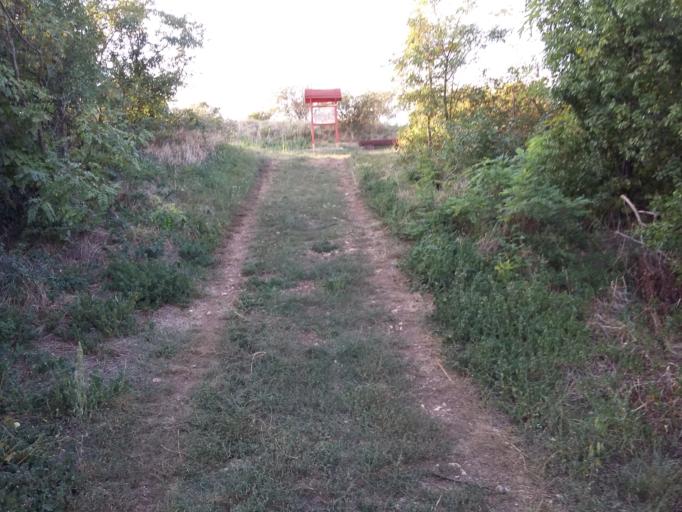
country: HU
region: Borsod-Abauj-Zemplen
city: Bekecs
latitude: 48.1559
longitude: 21.1717
